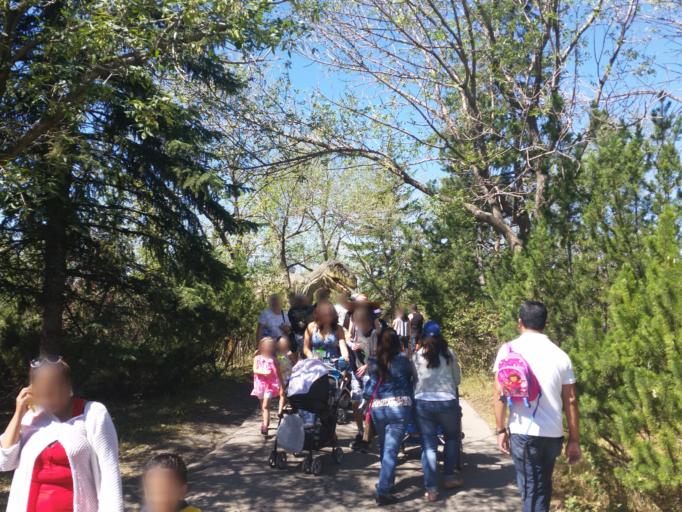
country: CA
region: Alberta
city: Calgary
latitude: 51.0462
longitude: -114.0271
